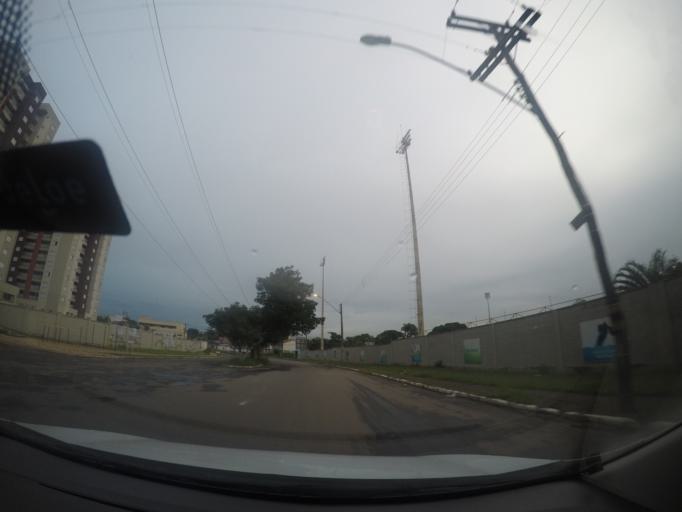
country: BR
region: Goias
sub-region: Goiania
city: Goiania
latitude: -16.6427
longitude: -49.2468
